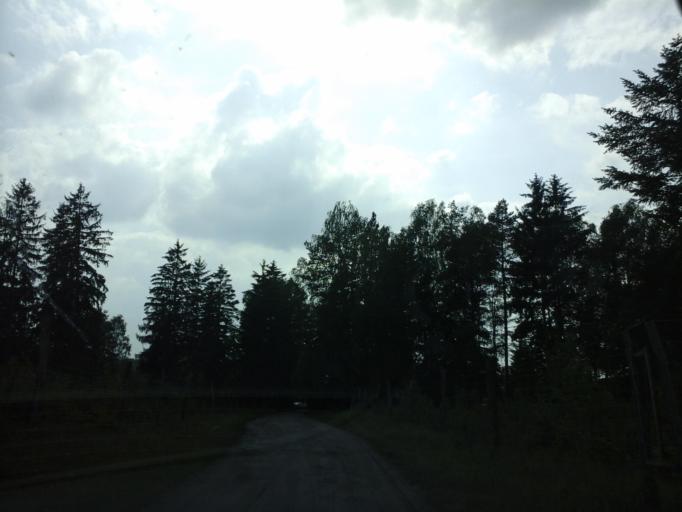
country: PL
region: West Pomeranian Voivodeship
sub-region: Powiat drawski
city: Kalisz Pomorski
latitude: 53.2082
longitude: 15.9735
